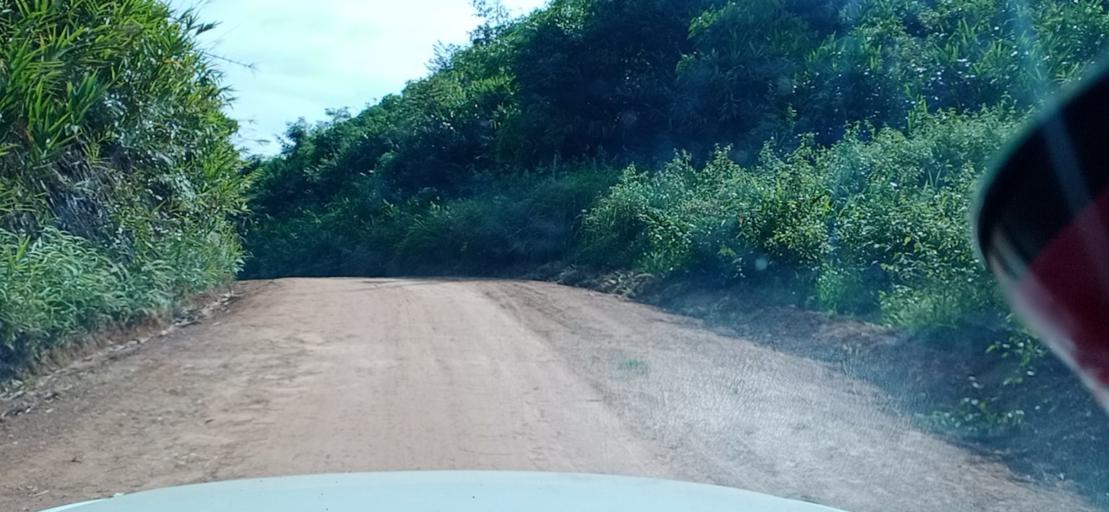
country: TH
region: Changwat Bueng Kan
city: Pak Khat
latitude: 18.6385
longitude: 103.2416
